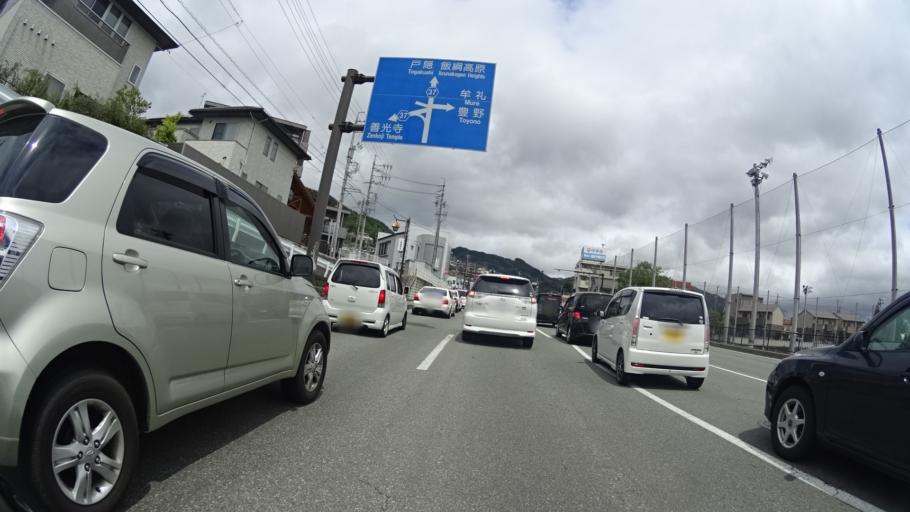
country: JP
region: Nagano
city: Nagano-shi
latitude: 36.6699
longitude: 138.1980
